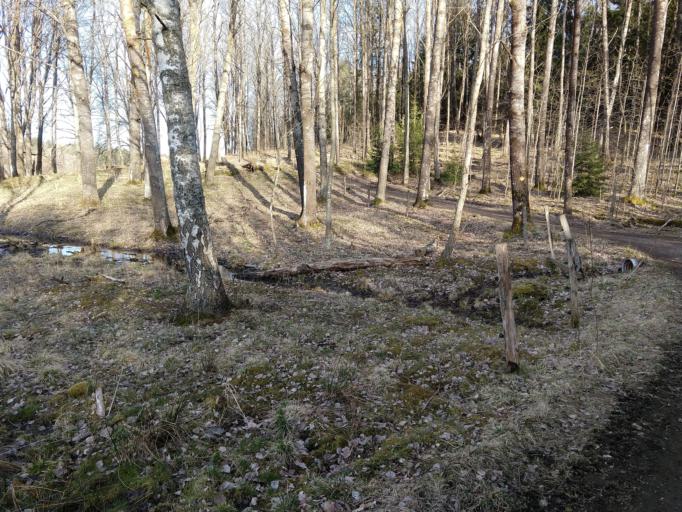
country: SE
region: Stockholm
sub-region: Huddinge Kommun
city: Huddinge
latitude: 59.2230
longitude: 17.9679
